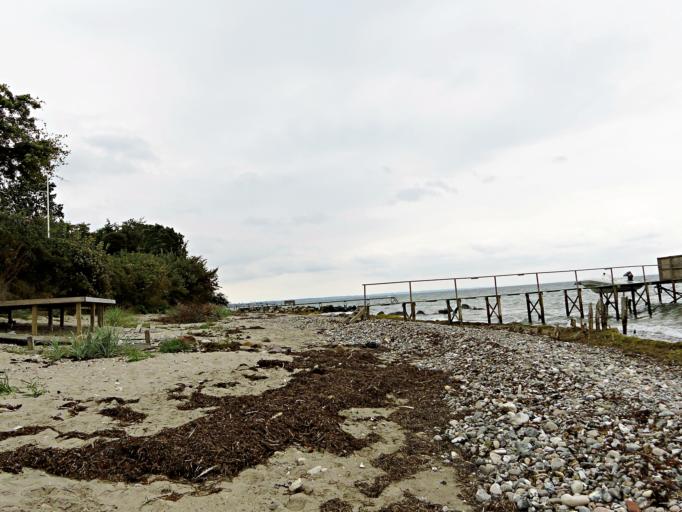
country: DK
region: Capital Region
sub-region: Rudersdal Kommune
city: Trorod
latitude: 55.8655
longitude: 12.5601
